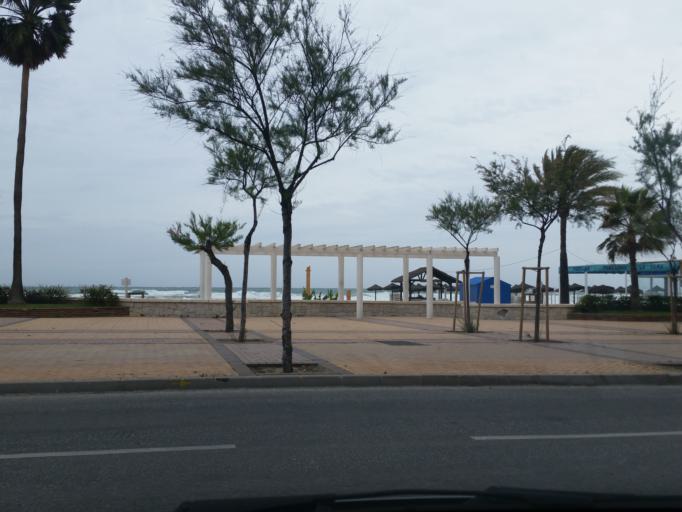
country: ES
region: Andalusia
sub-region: Provincia de Malaga
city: Fuengirola
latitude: 36.5553
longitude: -4.6115
